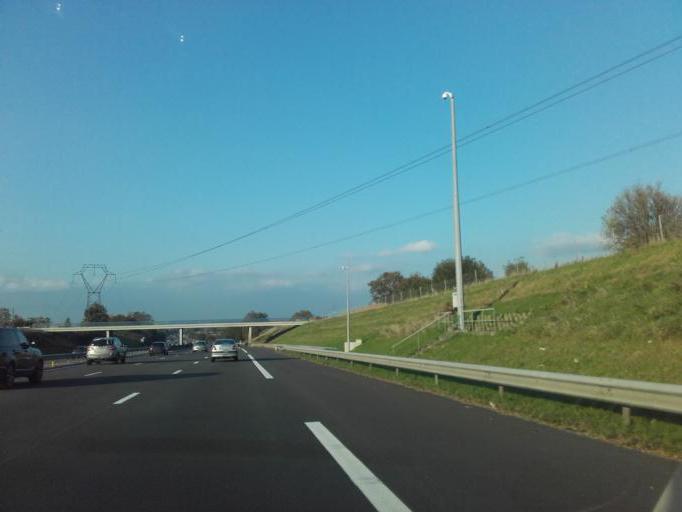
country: FR
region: Bourgogne
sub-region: Departement de Saone-et-Loire
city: Saint-Martin-Belle-Roche
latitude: 46.4269
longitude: 4.8684
